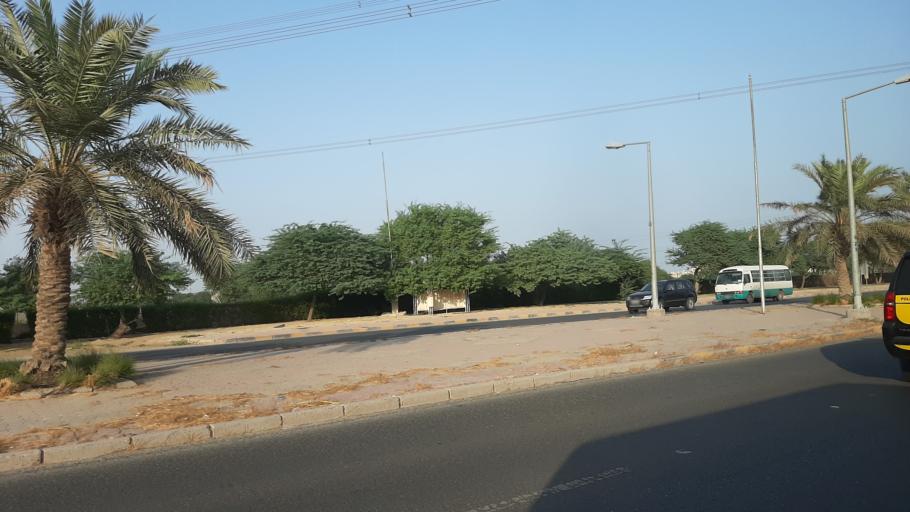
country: KW
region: Al Ahmadi
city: Al Ahmadi
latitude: 29.0942
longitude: 48.0916
